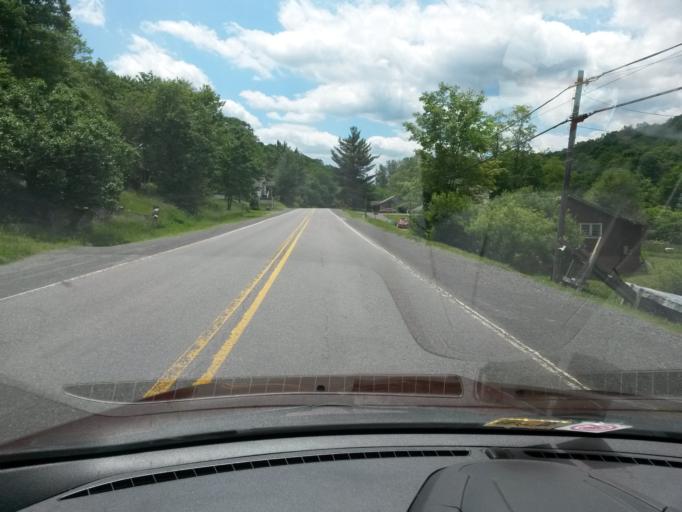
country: US
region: West Virginia
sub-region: Greenbrier County
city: Rainelle
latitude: 38.0439
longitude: -80.7235
